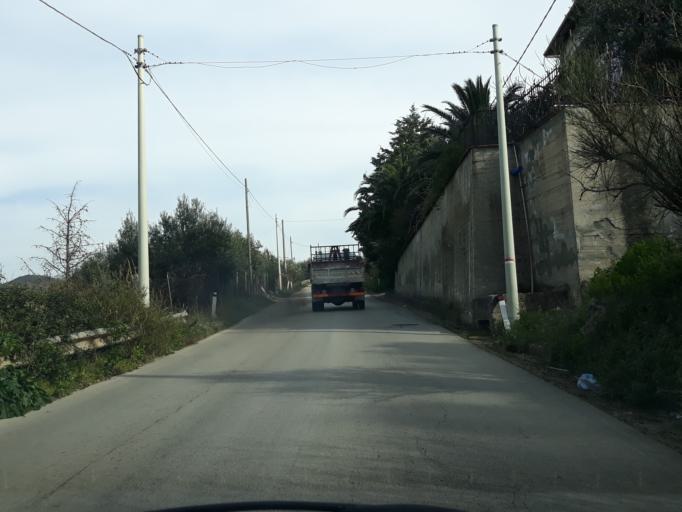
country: IT
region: Sicily
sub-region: Palermo
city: Piano Maglio-Blandino
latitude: 38.0427
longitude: 13.3172
